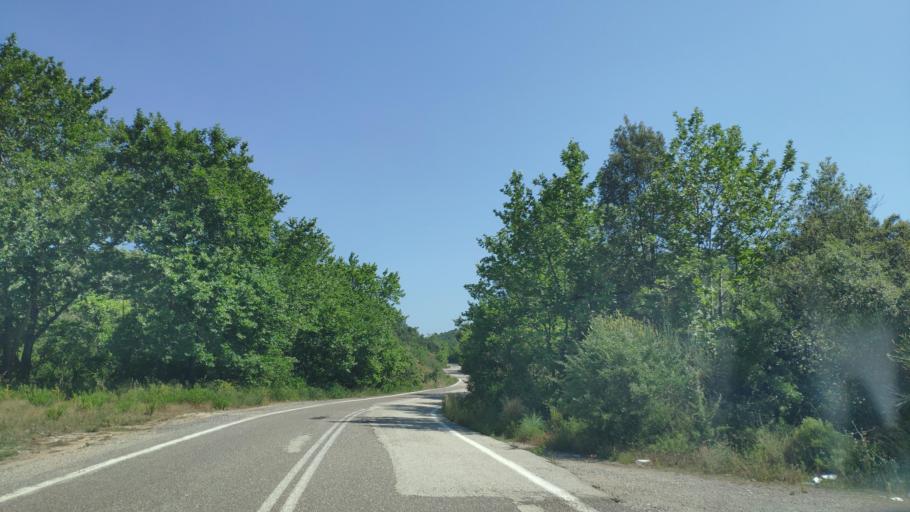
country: GR
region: West Greece
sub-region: Nomos Aitolias kai Akarnanias
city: Lepenou
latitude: 38.7771
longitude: 21.3349
